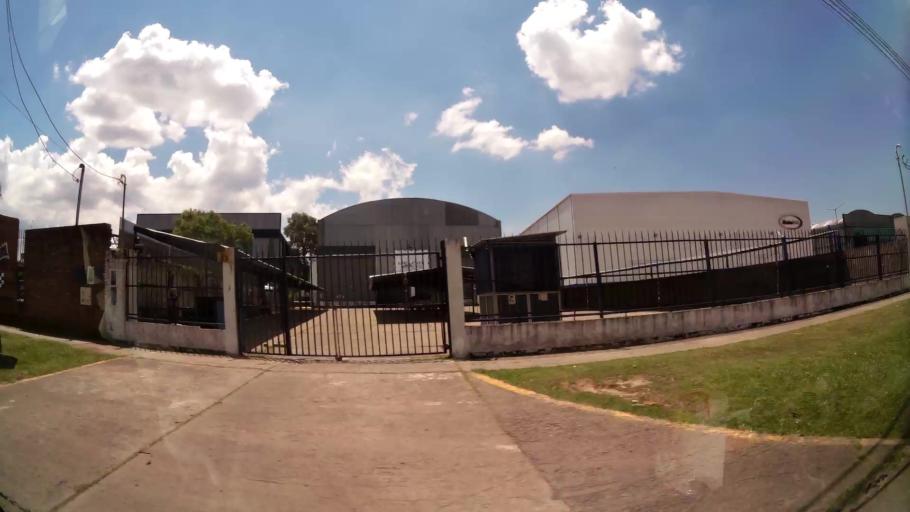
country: AR
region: Buenos Aires
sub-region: Partido de Tigre
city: Tigre
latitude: -34.4033
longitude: -58.6022
